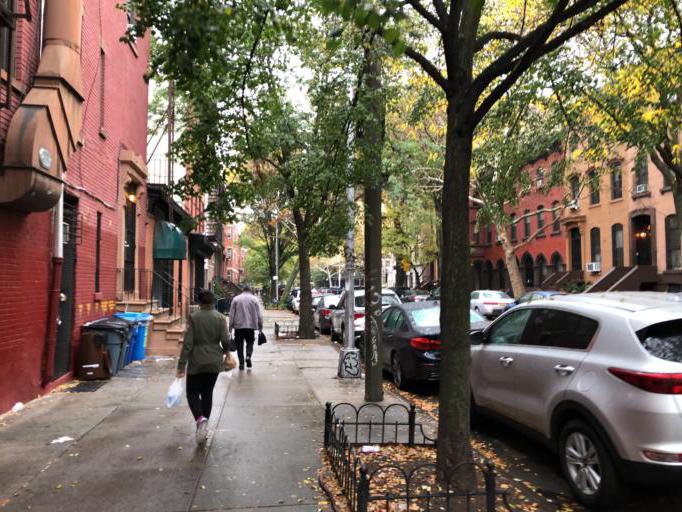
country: US
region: New York
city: New York City
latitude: 40.6874
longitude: -73.9767
